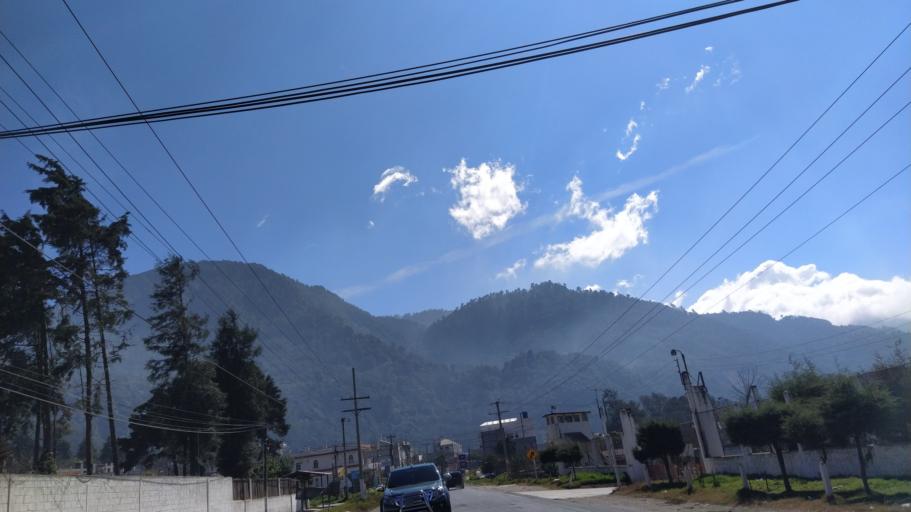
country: GT
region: Quetzaltenango
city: Cantel
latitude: 14.8096
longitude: -91.4479
